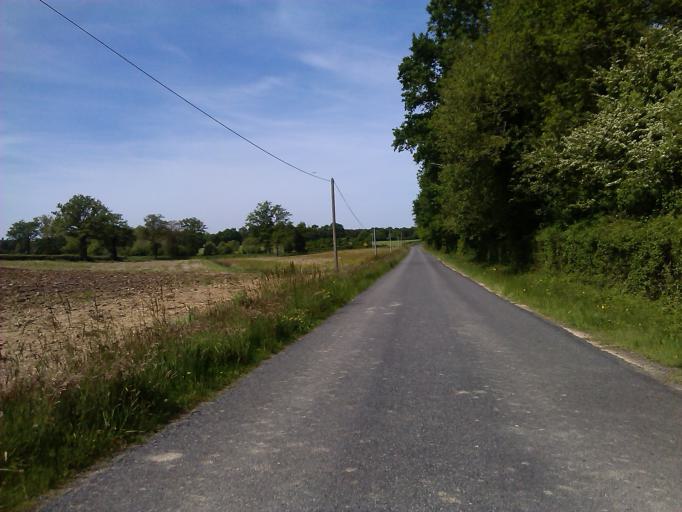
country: FR
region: Auvergne
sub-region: Departement de l'Allier
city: Lusigny
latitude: 46.5673
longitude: 3.4395
